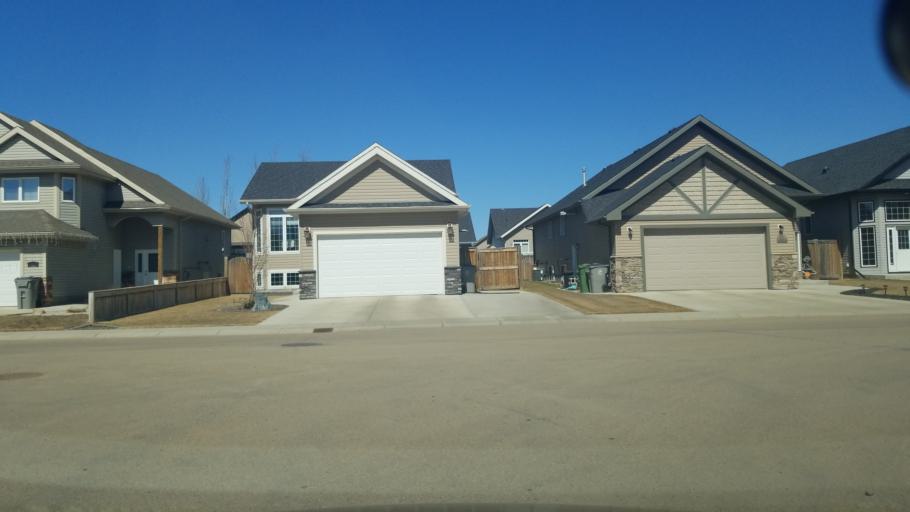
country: CA
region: Saskatchewan
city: Lloydminster
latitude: 53.2505
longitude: -110.0184
